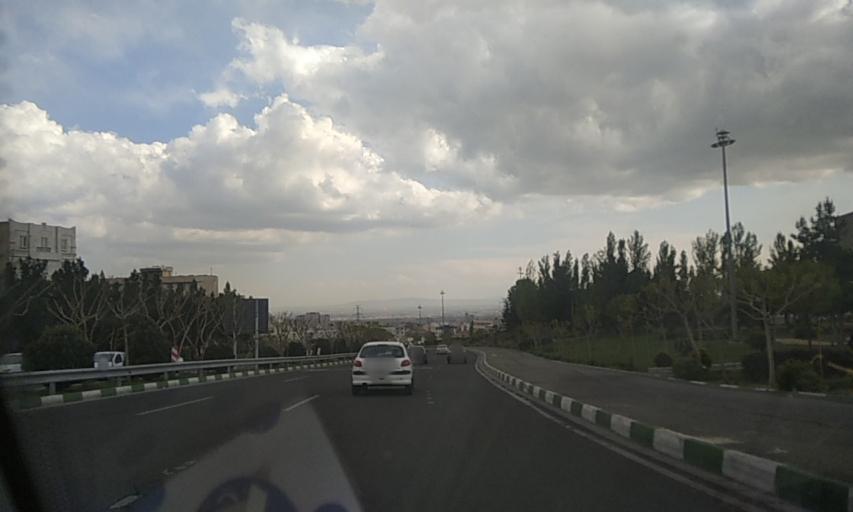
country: IR
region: Tehran
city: Tajrish
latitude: 35.7770
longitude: 51.3199
